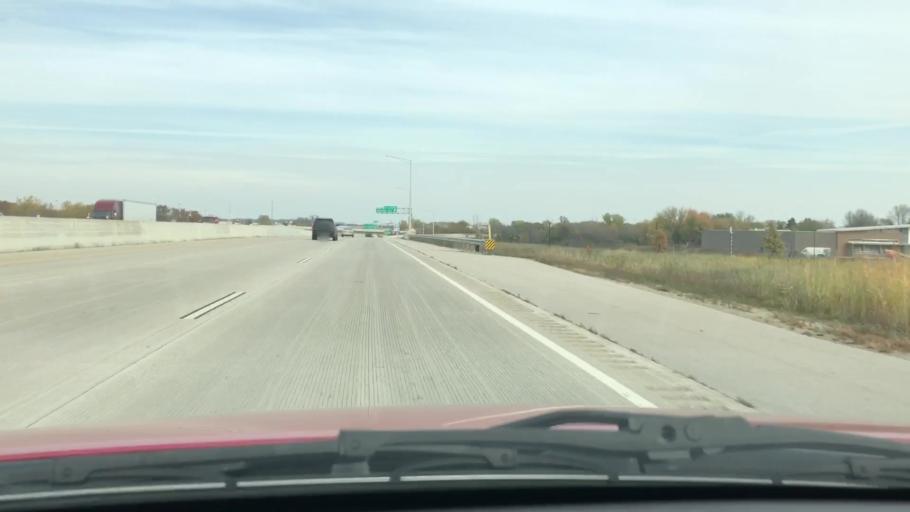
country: US
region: Wisconsin
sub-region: Brown County
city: De Pere
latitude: 44.4516
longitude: -88.0904
